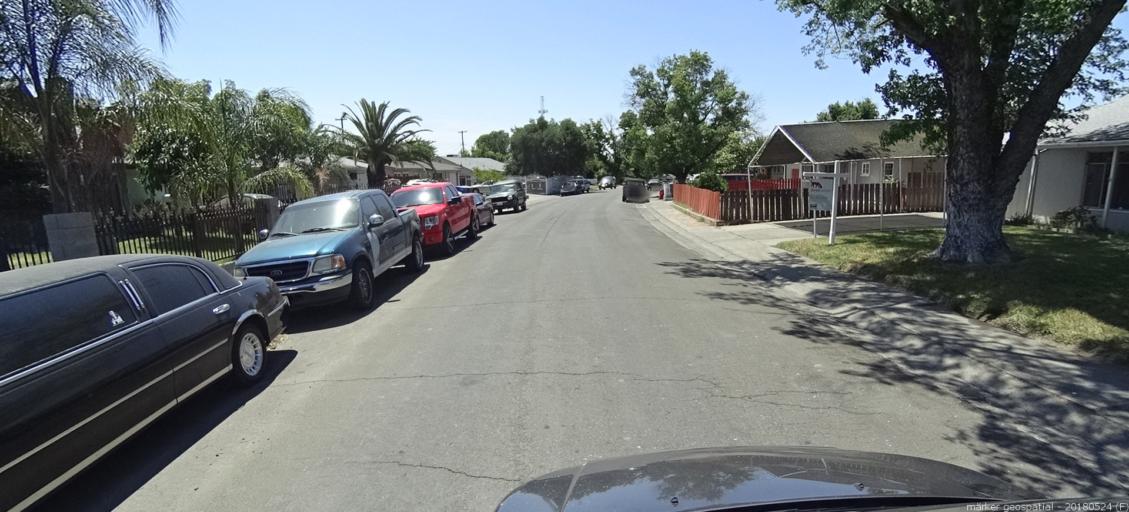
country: US
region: California
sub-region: Sacramento County
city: Sacramento
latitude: 38.6208
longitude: -121.4501
